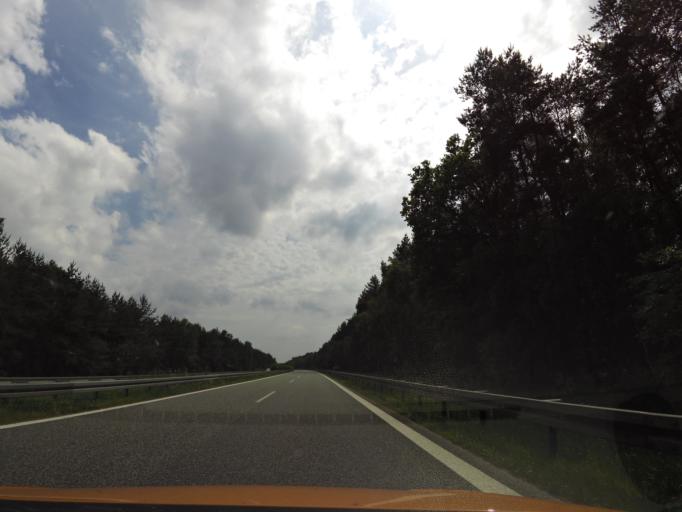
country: DE
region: Mecklenburg-Vorpommern
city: Mirow
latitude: 53.5021
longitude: 11.4745
